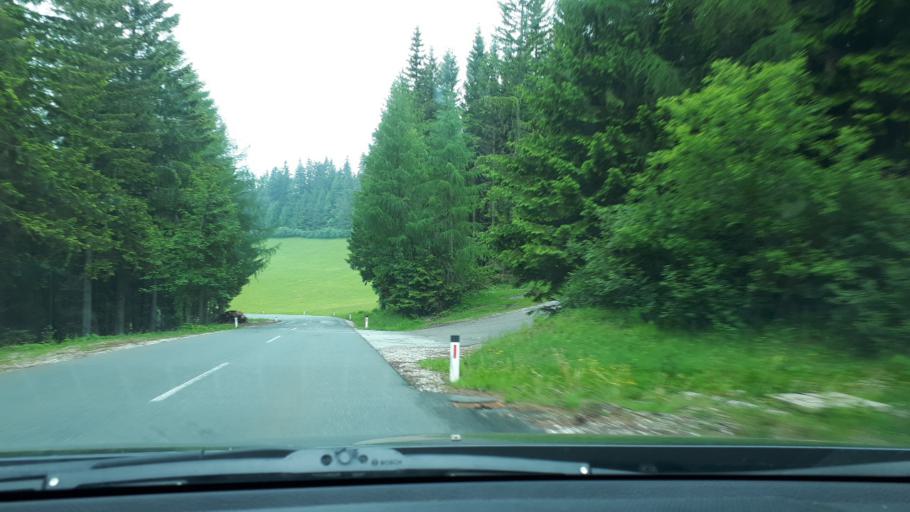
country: AT
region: Styria
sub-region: Politischer Bezirk Voitsberg
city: Modriach
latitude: 46.9302
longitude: 15.0025
